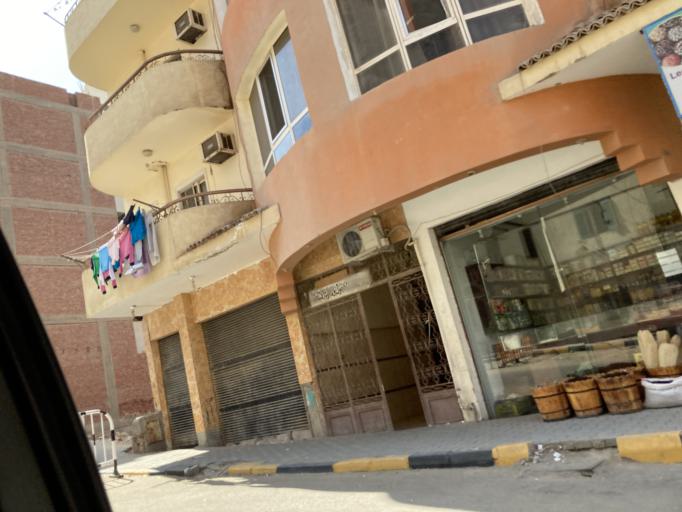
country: EG
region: Red Sea
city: Hurghada
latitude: 27.2509
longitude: 33.8317
